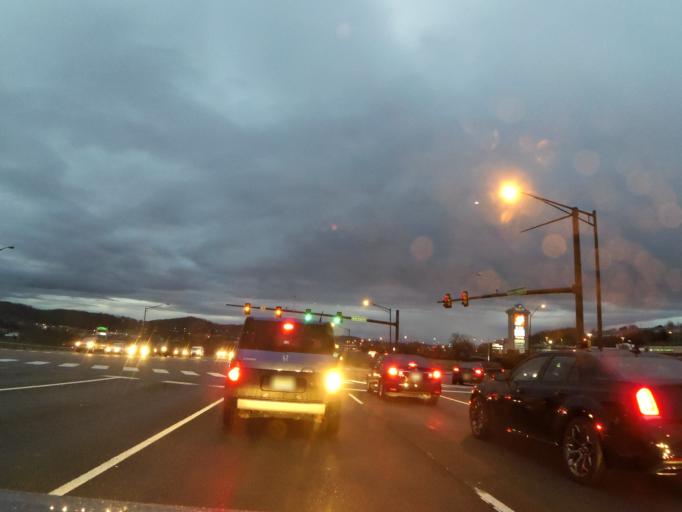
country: US
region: Tennessee
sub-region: Washington County
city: Midway
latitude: 36.3420
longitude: -82.4043
